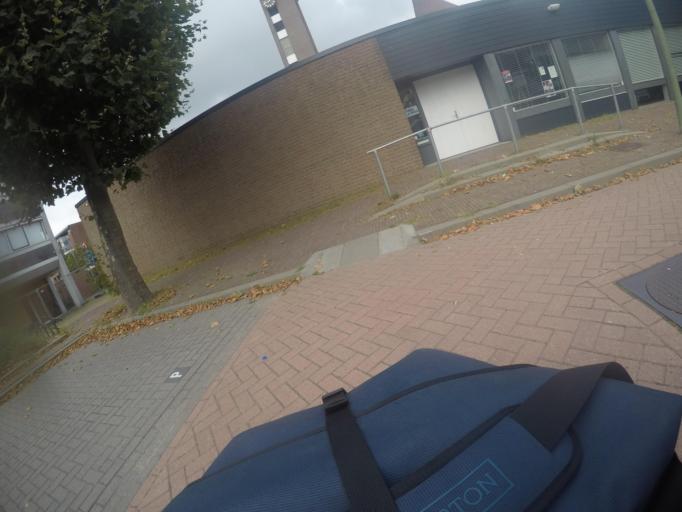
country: NL
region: Flevoland
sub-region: Gemeente Almere
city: Almere Stad
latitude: 52.3356
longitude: 5.2208
